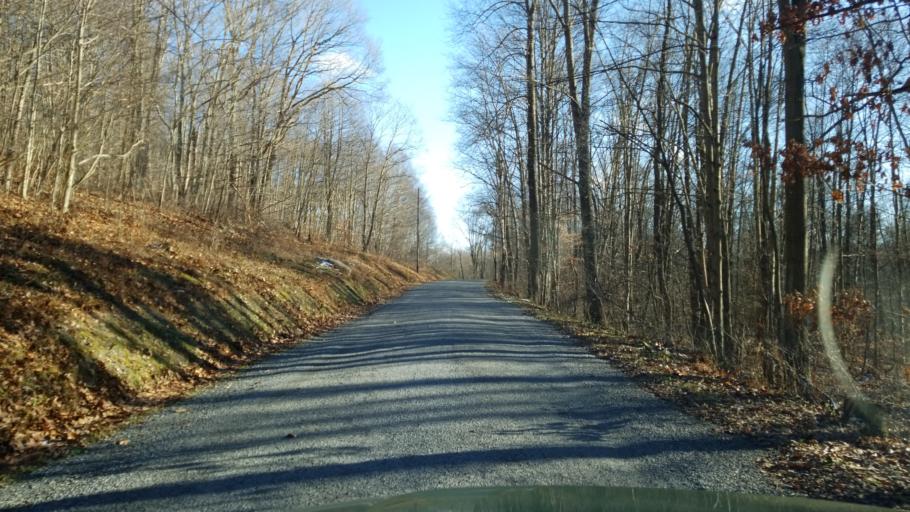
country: US
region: Pennsylvania
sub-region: Jefferson County
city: Brockway
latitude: 41.2744
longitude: -78.8146
